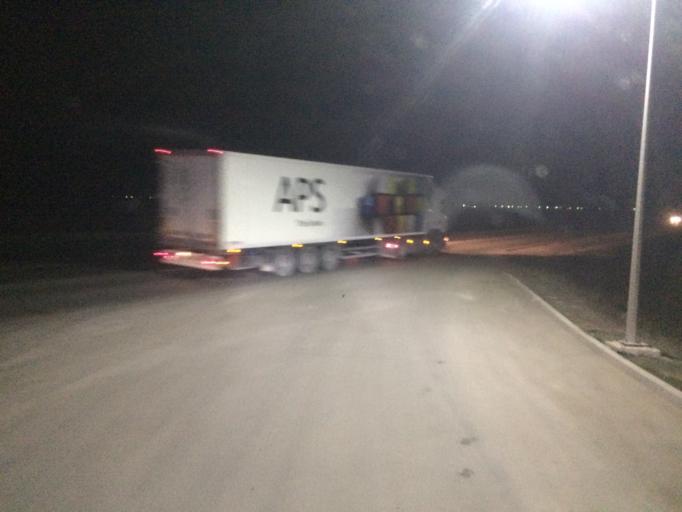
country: KZ
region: Batys Qazaqstan
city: Oral
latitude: 51.2195
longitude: 51.2789
